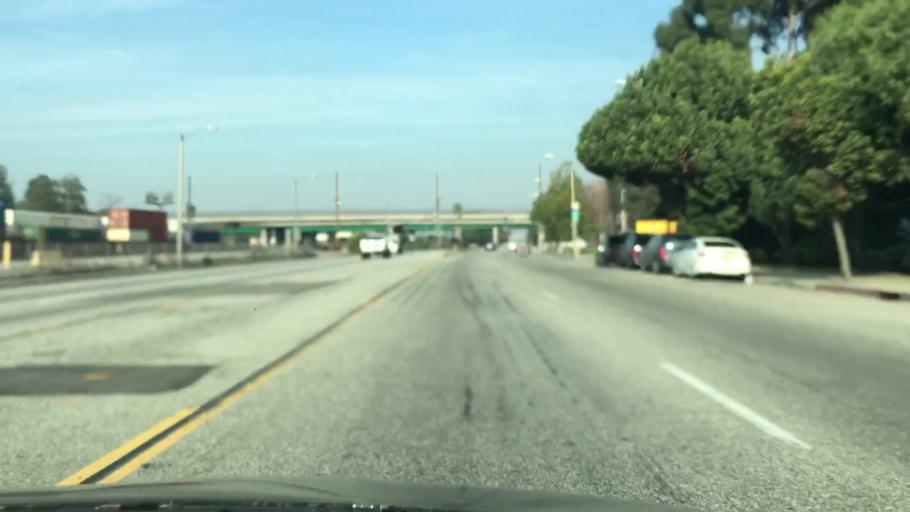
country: US
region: California
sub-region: Los Angeles County
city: Carson
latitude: 33.8219
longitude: -118.2297
